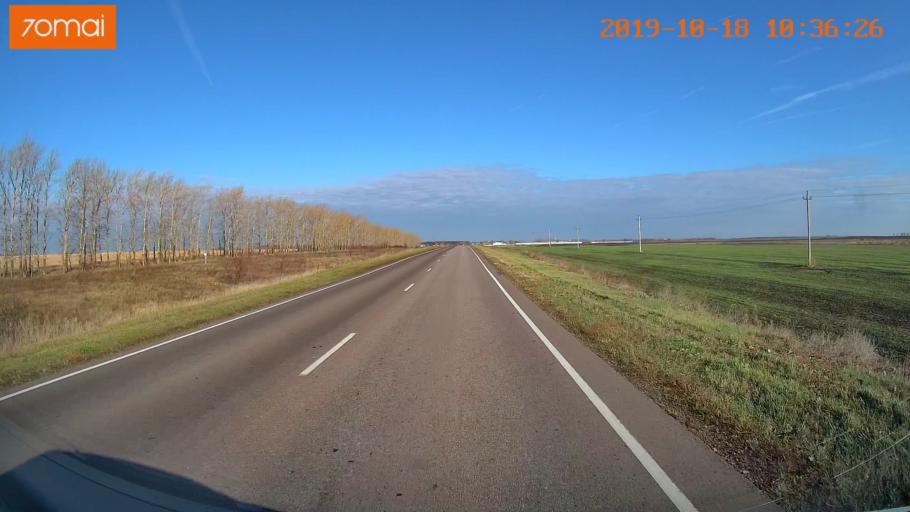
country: RU
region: Tula
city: Kurkino
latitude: 53.5483
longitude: 38.6257
